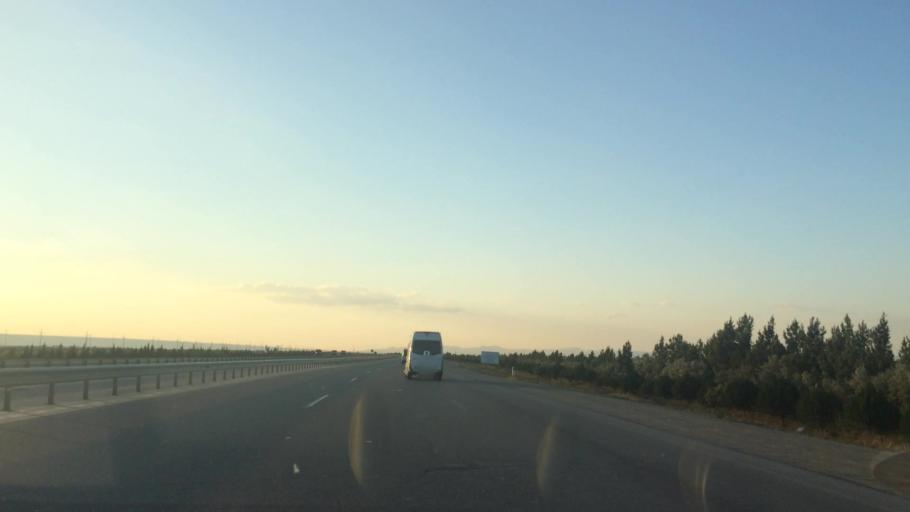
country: AZ
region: Baki
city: Qobustan
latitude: 39.9768
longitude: 49.2452
